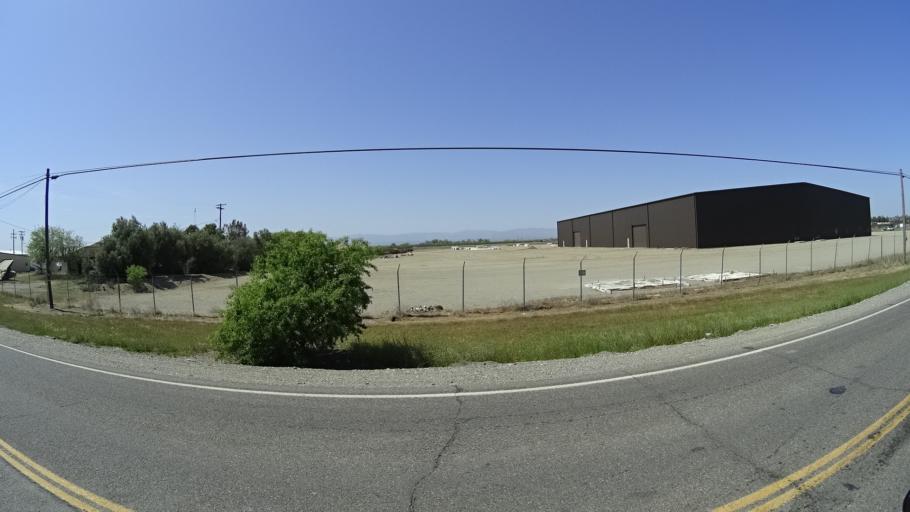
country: US
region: California
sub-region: Glenn County
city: Orland
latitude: 39.6881
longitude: -122.1968
